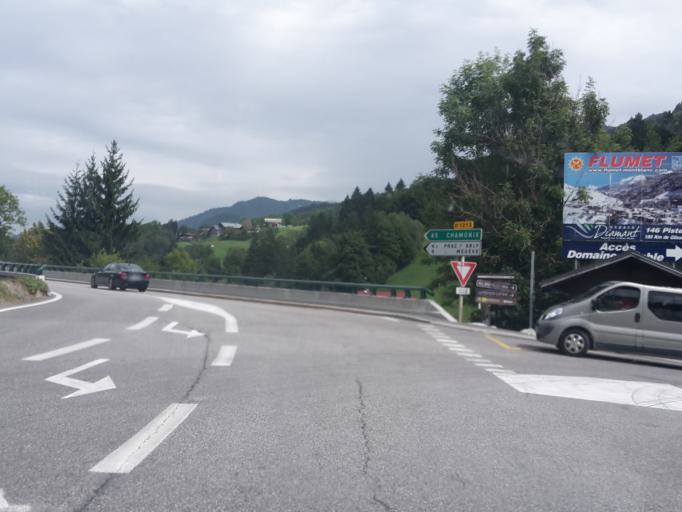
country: FR
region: Rhone-Alpes
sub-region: Departement de la Haute-Savoie
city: Praz-sur-Arly
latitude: 45.8213
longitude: 6.5309
